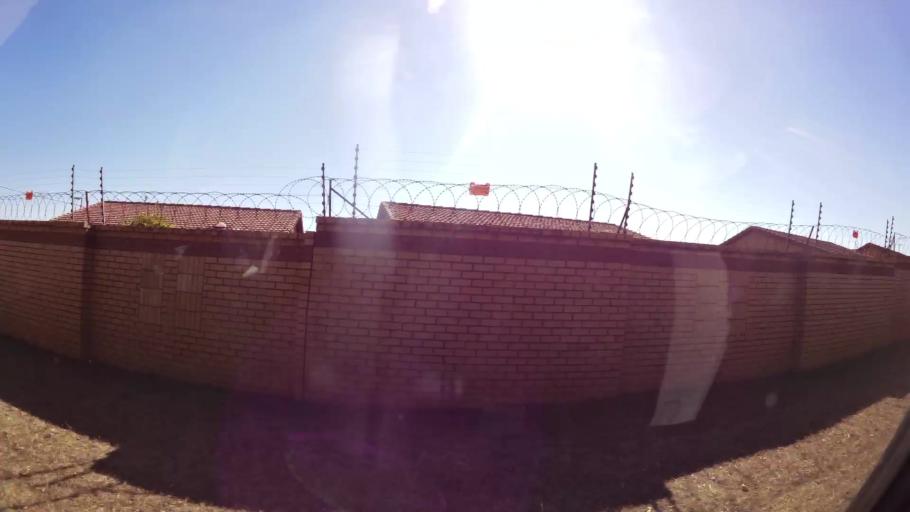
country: ZA
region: Gauteng
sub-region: City of Johannesburg Metropolitan Municipality
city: Roodepoort
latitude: -26.1230
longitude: 27.8452
